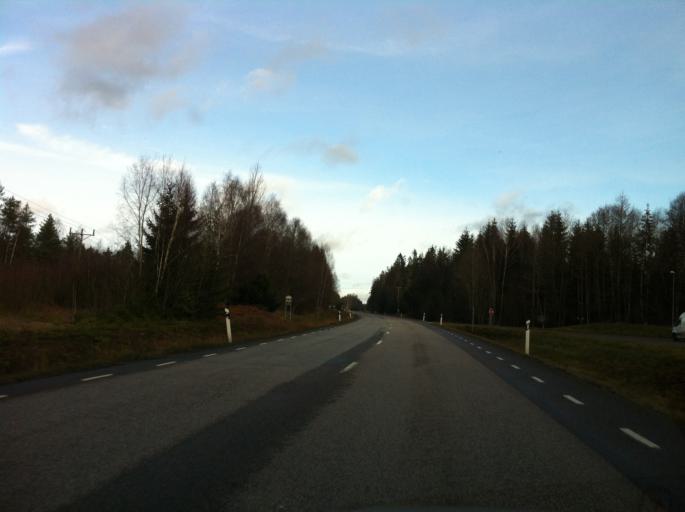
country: SE
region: Kronoberg
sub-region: Almhults Kommun
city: AElmhult
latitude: 56.5776
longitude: 14.1875
